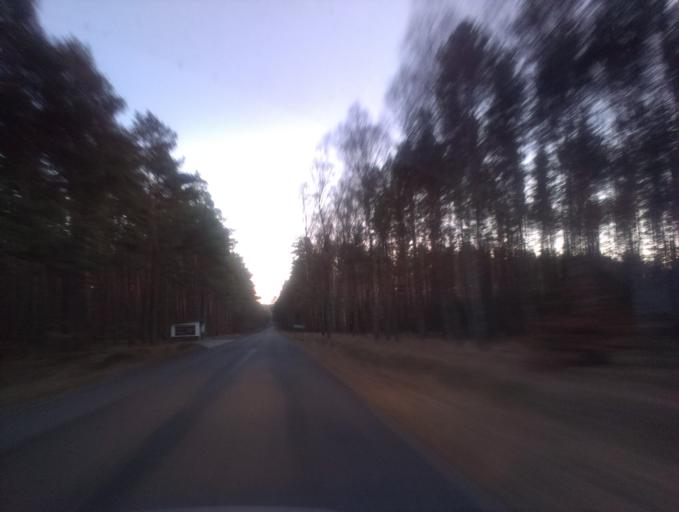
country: PL
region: Greater Poland Voivodeship
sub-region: Powiat zlotowski
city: Okonek
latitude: 53.5024
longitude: 16.9796
